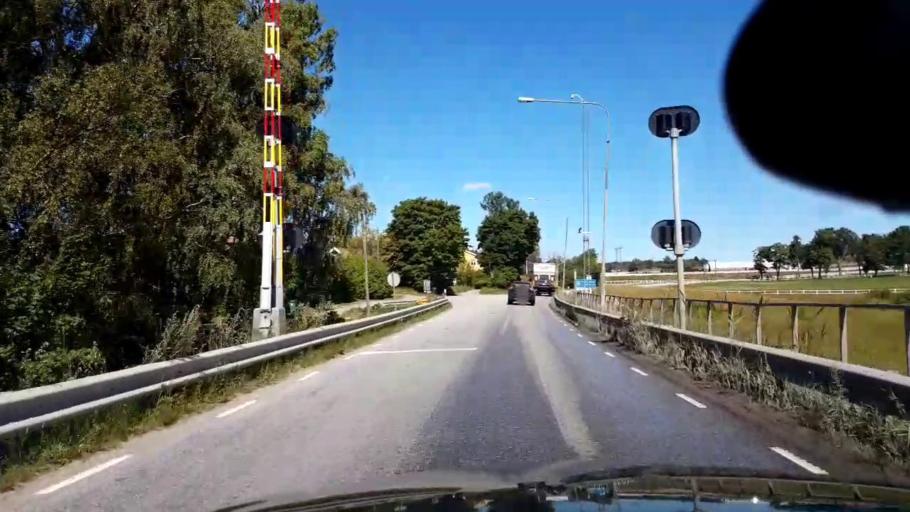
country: SE
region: Uppsala
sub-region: Habo Kommun
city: Balsta
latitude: 59.6407
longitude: 17.6090
